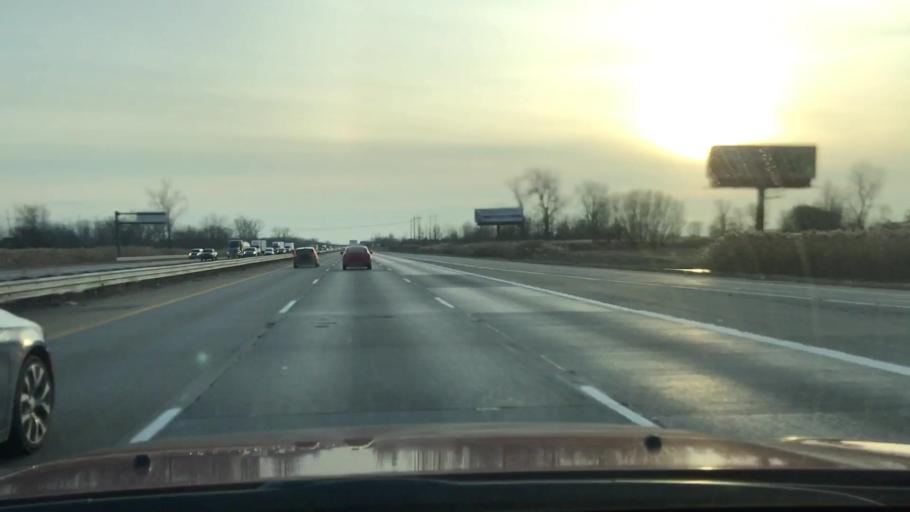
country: US
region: Michigan
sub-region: Monroe County
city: Luna Pier
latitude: 41.8059
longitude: -83.4533
